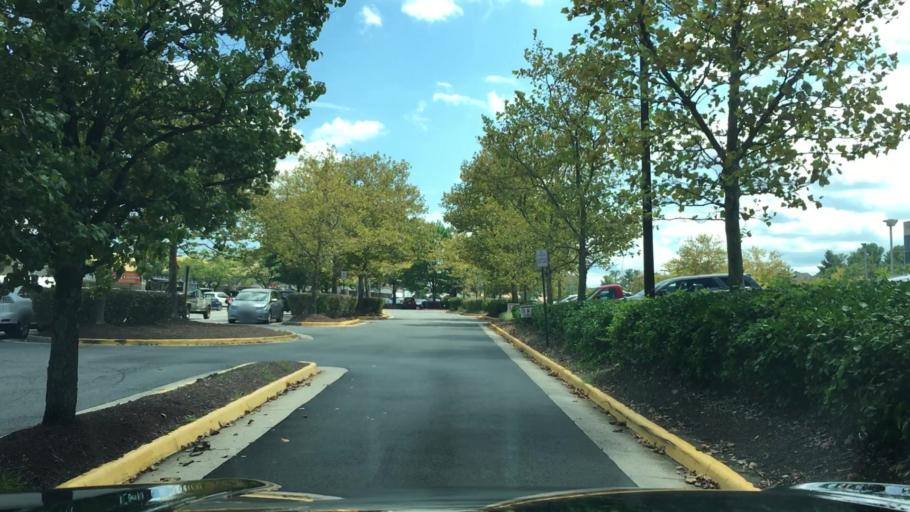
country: US
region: Virginia
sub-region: Fairfax County
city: Centreville
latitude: 38.8375
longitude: -77.4287
